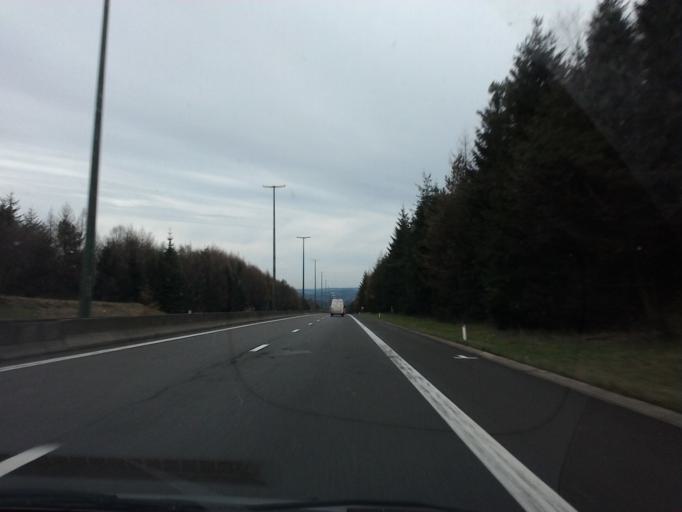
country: BE
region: Wallonia
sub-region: Province du Luxembourg
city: Manhay
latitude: 50.2673
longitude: 5.7263
